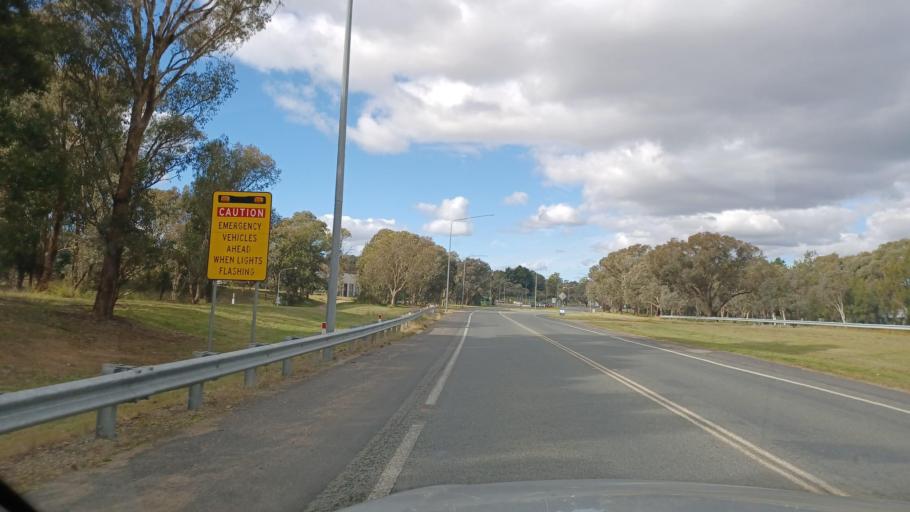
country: AU
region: Australian Capital Territory
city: Belconnen
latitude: -35.2064
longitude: 149.0308
